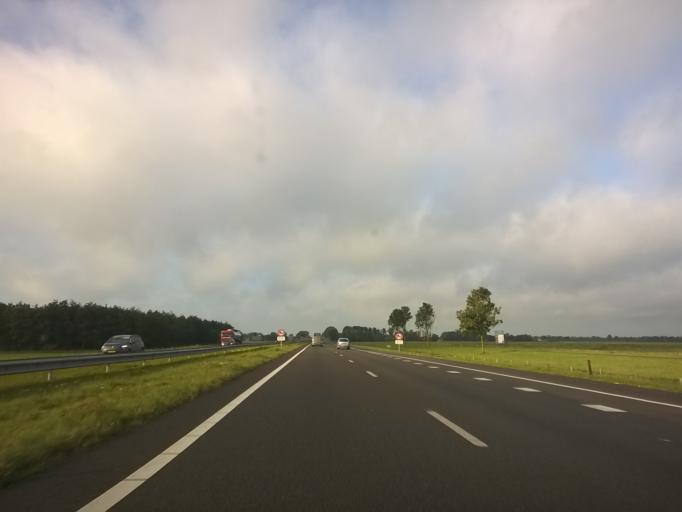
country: NL
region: Groningen
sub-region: Gemeente Grootegast
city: Grootegast
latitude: 53.1500
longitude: 6.2563
